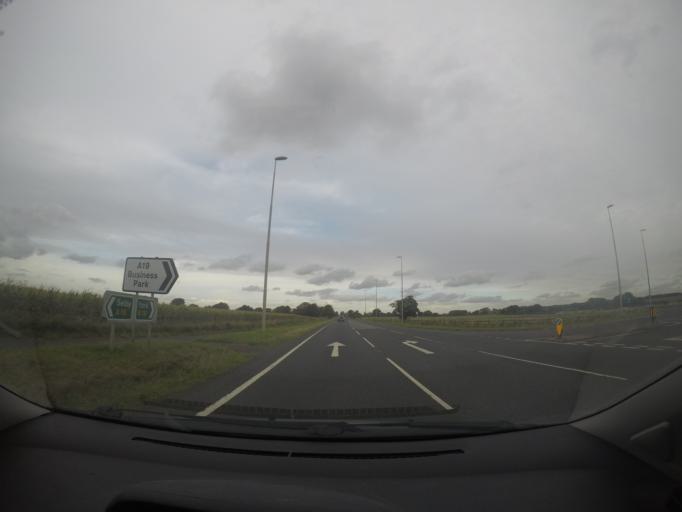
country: GB
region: England
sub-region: North Yorkshire
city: Barlby
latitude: 53.8165
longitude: -1.0433
